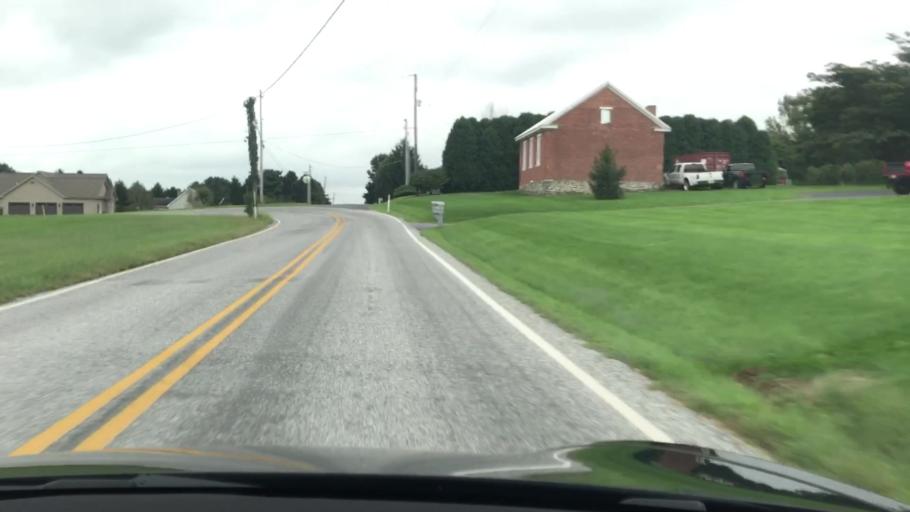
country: US
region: Pennsylvania
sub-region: York County
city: Dillsburg
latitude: 40.0613
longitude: -77.0844
